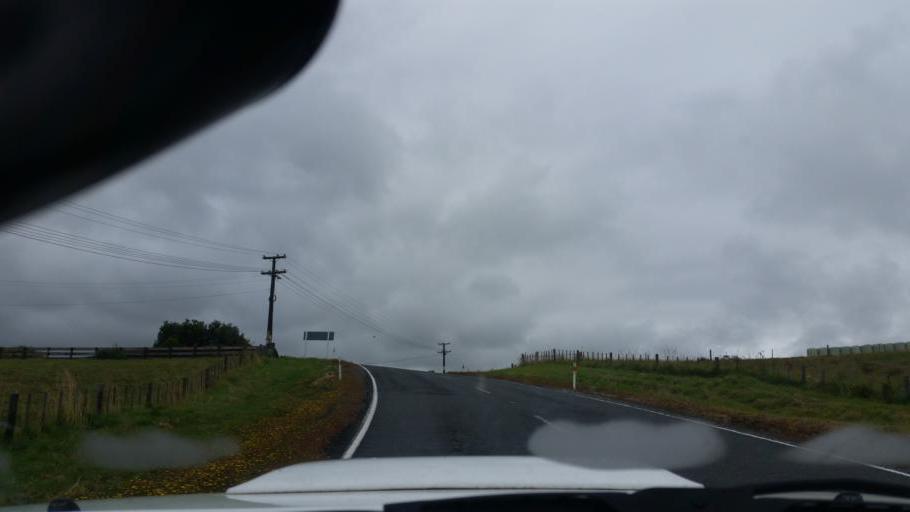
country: NZ
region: Auckland
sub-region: Auckland
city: Wellsford
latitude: -36.1584
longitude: 174.4583
